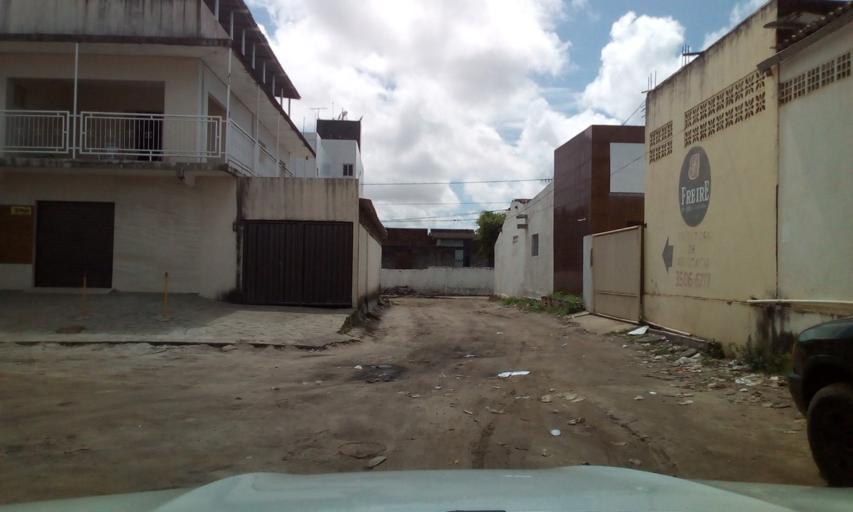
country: BR
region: Paraiba
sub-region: Joao Pessoa
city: Joao Pessoa
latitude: -7.1795
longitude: -34.8714
